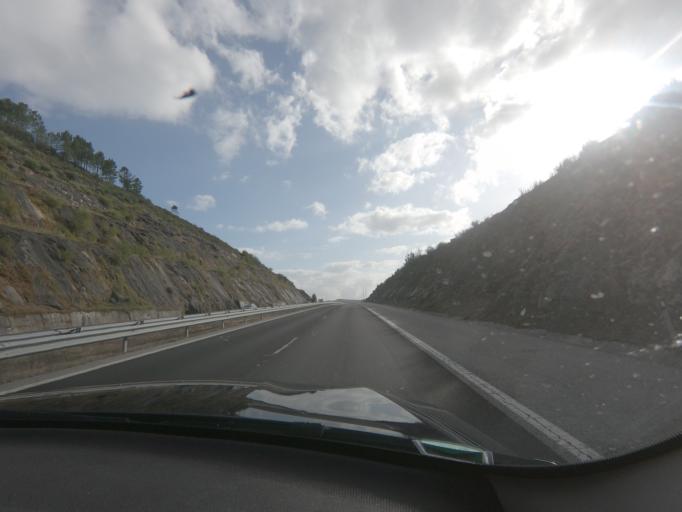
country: PT
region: Viseu
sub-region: Castro Daire
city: Castro Daire
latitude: 40.8383
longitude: -7.9317
